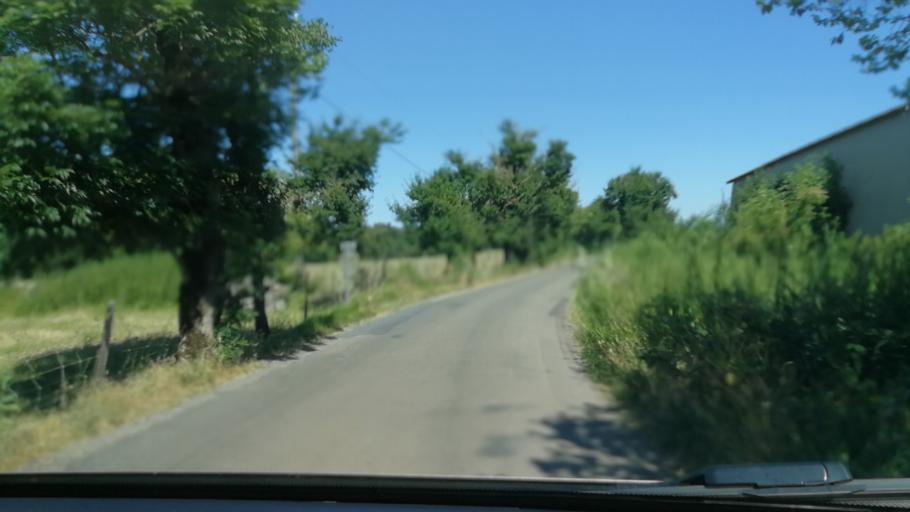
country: FR
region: Midi-Pyrenees
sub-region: Departement de l'Aveyron
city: Salles-la-Source
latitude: 44.4230
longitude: 2.5453
